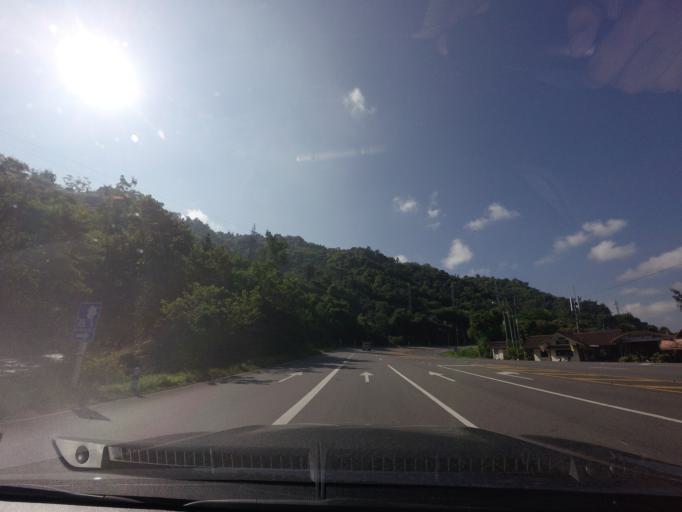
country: TH
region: Phetchabun
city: Khao Kho
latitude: 16.7820
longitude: 101.0844
